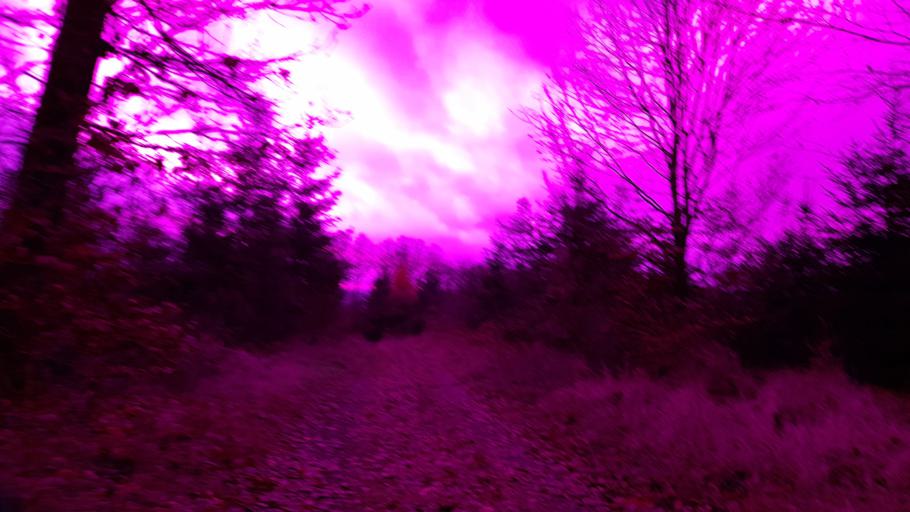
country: DE
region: Rheinland-Pfalz
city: Dasburg
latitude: 50.0648
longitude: 6.1080
